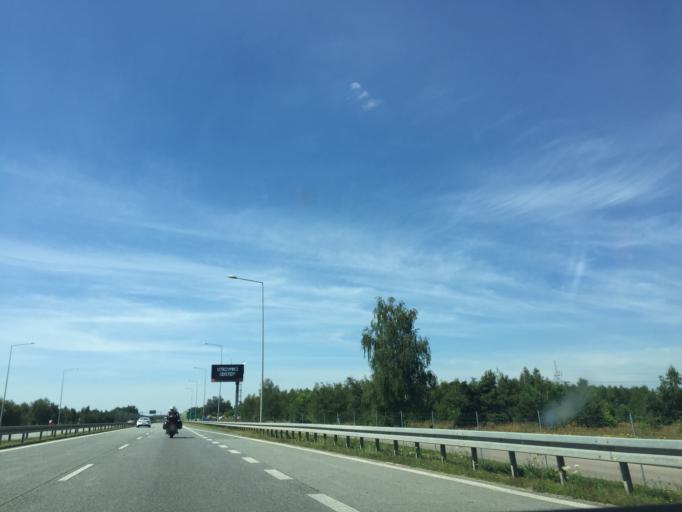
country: PL
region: Lodz Voivodeship
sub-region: Powiat tomaszowski
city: Tomaszow Mazowiecki
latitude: 51.5481
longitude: 19.9833
